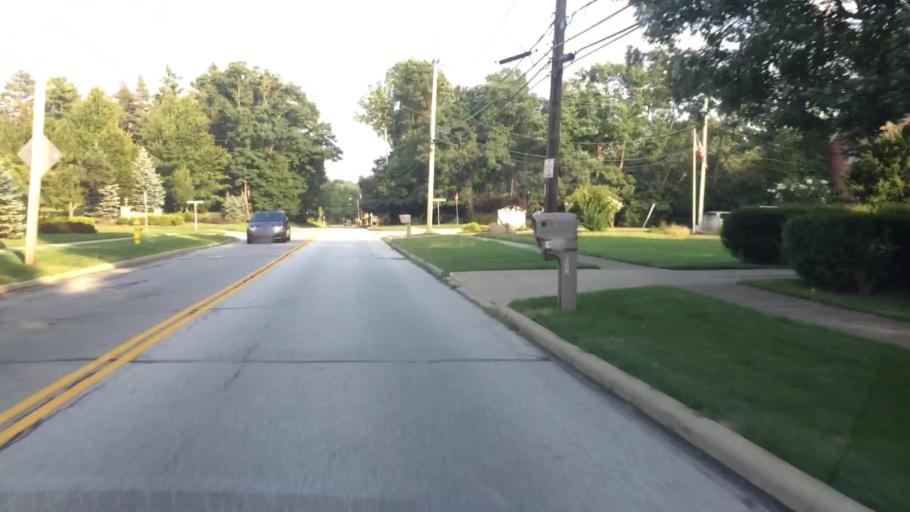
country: US
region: Ohio
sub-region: Cuyahoga County
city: Brecksville
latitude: 41.3307
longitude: -81.6408
